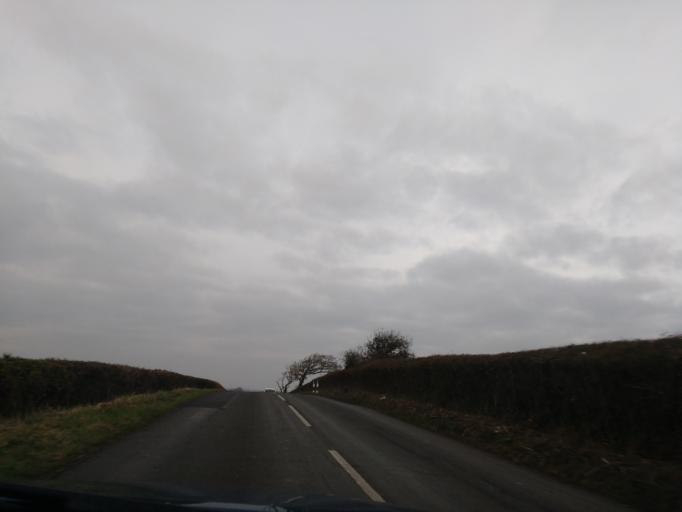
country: GB
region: England
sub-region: Isle of Wight
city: Northwood
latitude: 50.7282
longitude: -1.3534
